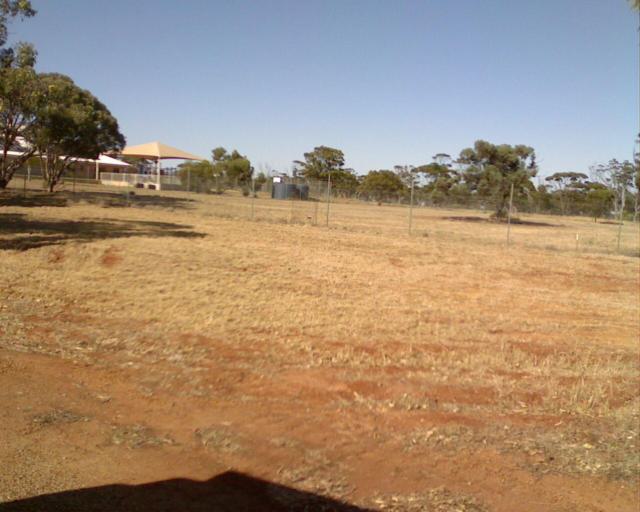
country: AU
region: Western Australia
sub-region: Wongan-Ballidu
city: Wongan Hills
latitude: -30.2821
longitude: 116.6558
